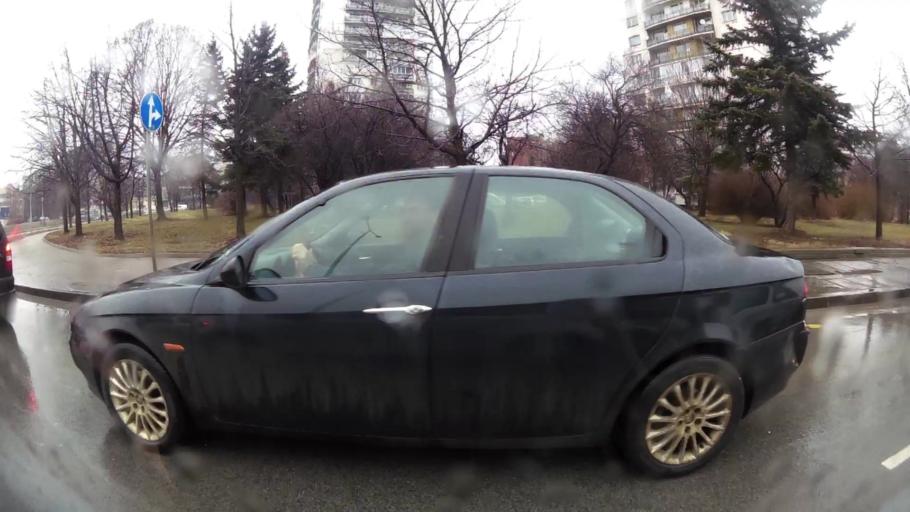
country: BG
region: Sofia-Capital
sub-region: Stolichna Obshtina
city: Sofia
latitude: 42.6506
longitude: 23.3784
